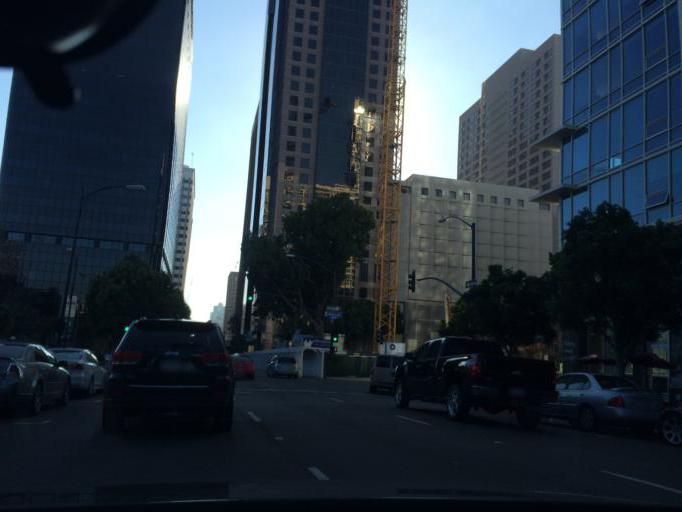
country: US
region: California
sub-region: San Diego County
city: San Diego
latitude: 32.7178
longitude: -117.1560
